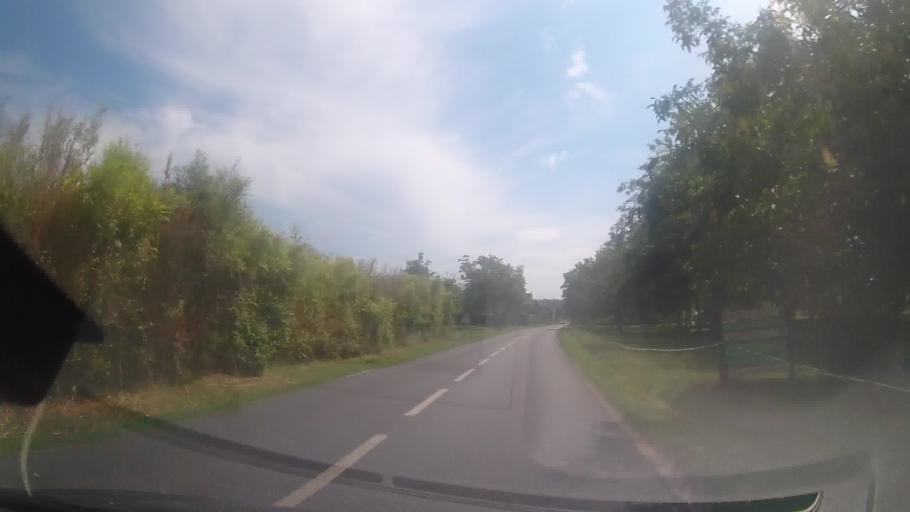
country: FR
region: Aquitaine
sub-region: Departement de la Dordogne
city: Cenac-et-Saint-Julien
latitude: 44.8235
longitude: 1.1869
